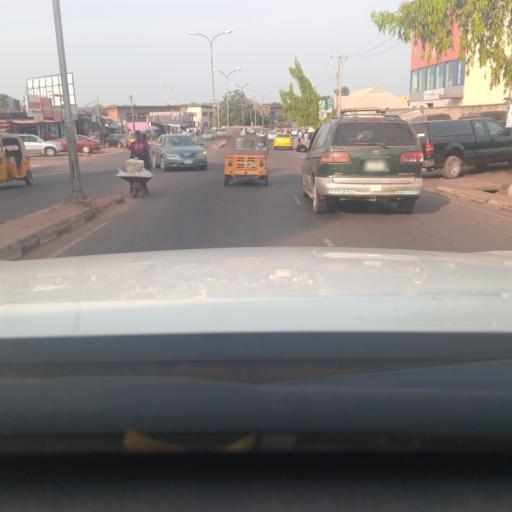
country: NG
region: Enugu
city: Enugu
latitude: 6.4518
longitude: 7.5032
